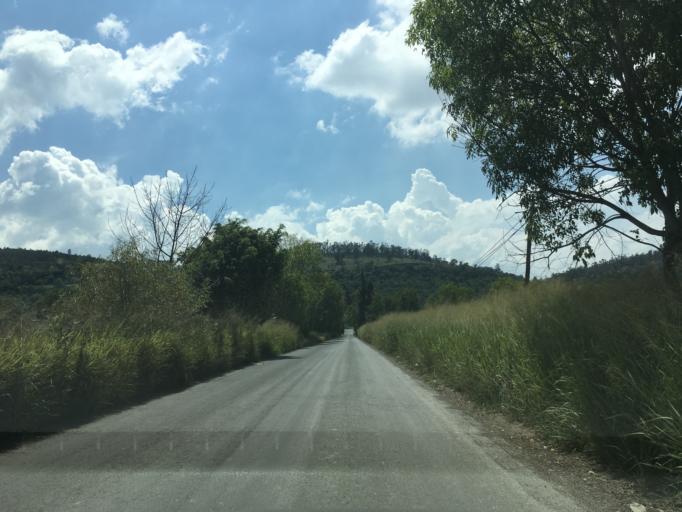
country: MX
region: Michoacan
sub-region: Morelia
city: La Mintzita (Piedra Dura)
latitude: 19.6446
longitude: -101.2660
